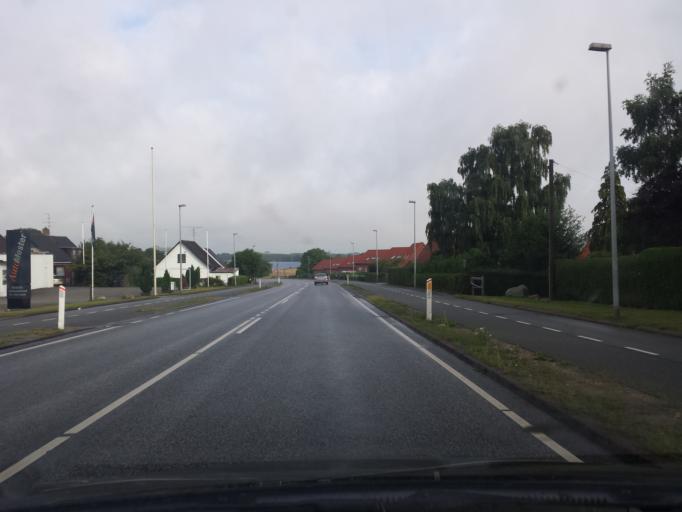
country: DK
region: South Denmark
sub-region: Sonderborg Kommune
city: Guderup
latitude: 55.0296
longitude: 9.8295
